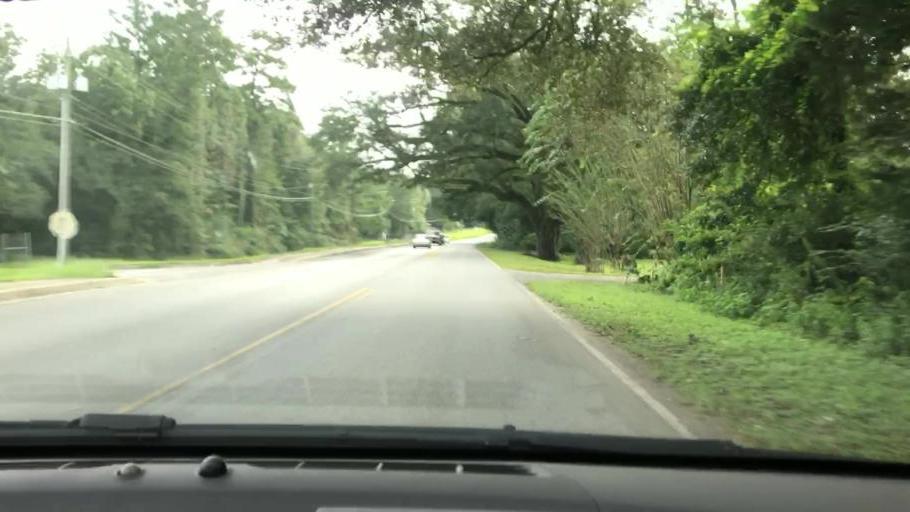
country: US
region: Florida
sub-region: Jackson County
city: Marianna
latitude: 30.7674
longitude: -85.2489
